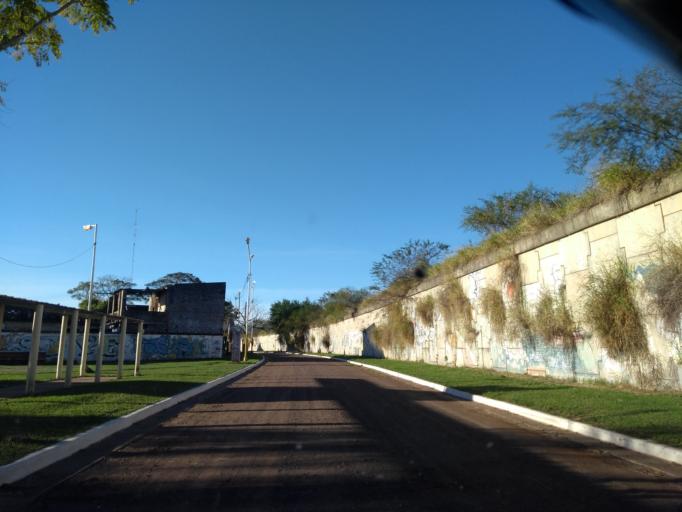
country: AR
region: Chaco
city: Barranqueras
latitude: -27.4892
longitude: -58.9262
